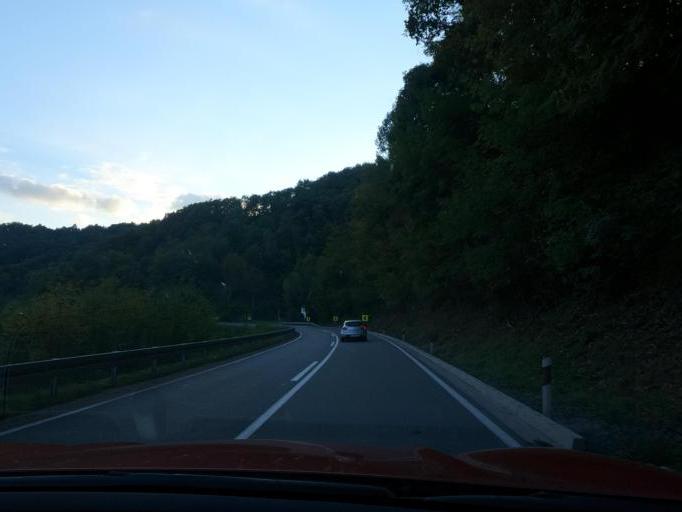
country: RS
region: Central Serbia
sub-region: Moravicki Okrug
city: Lucani
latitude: 43.8831
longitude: 20.1132
